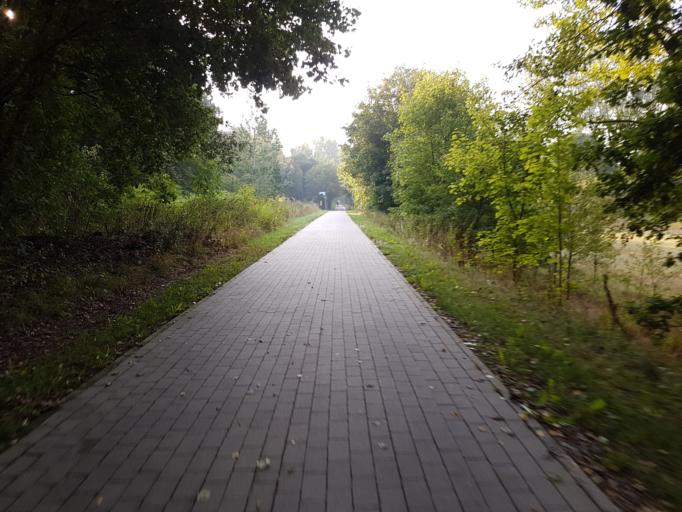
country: DE
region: Saxony
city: Wittgensdorf
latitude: 50.8800
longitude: 12.8951
